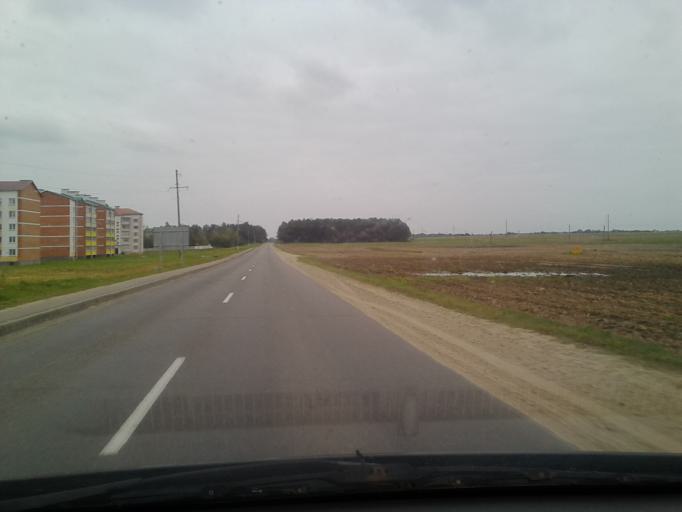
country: BY
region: Vitebsk
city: Pastavy
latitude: 55.1125
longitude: 26.8770
